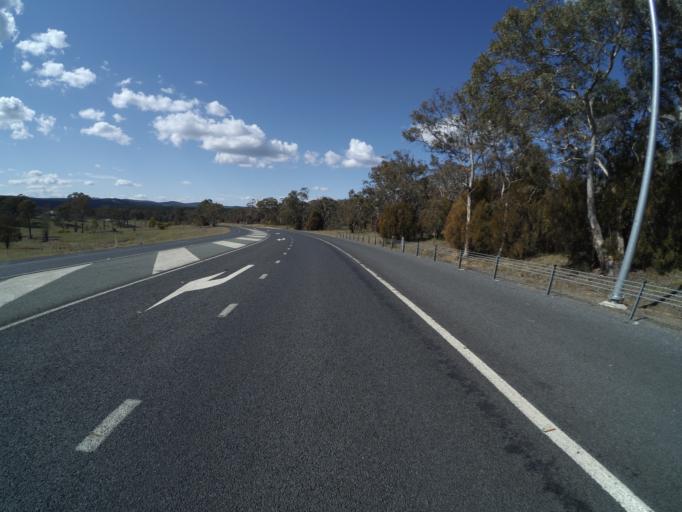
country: AU
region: New South Wales
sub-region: Queanbeyan
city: Queanbeyan
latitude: -35.3440
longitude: 149.2817
